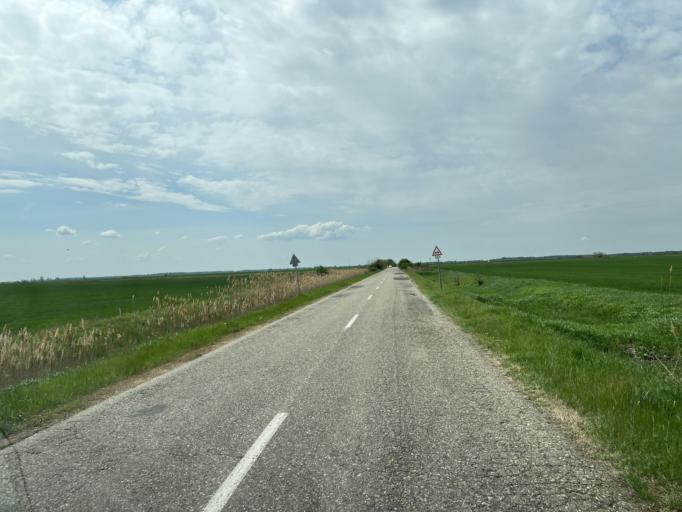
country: HU
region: Pest
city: Tortel
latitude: 47.1481
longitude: 19.9618
